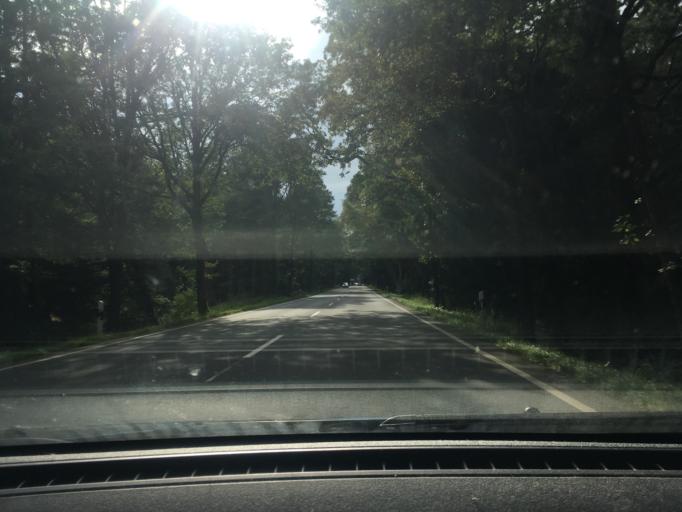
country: DE
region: Lower Saxony
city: Sprakensehl
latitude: 52.8082
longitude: 10.4265
